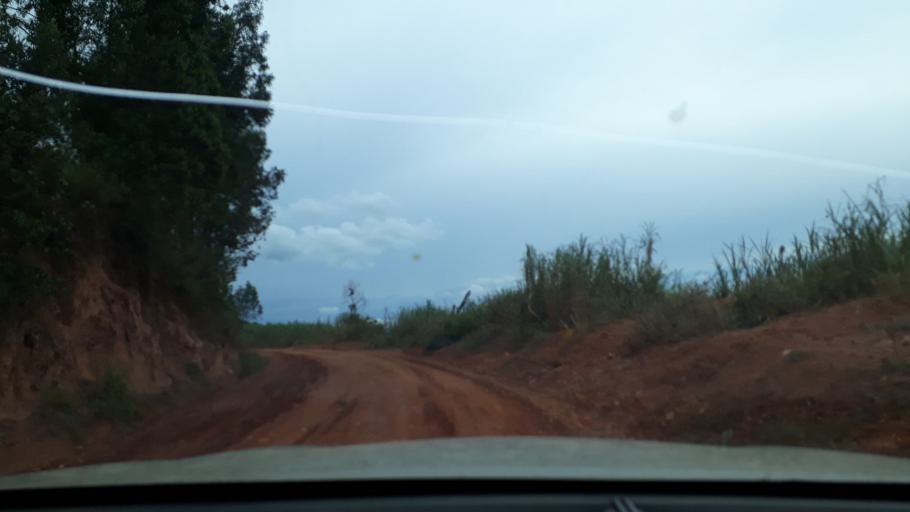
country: CD
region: Eastern Province
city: Bunia
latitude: 1.7741
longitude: 30.3918
